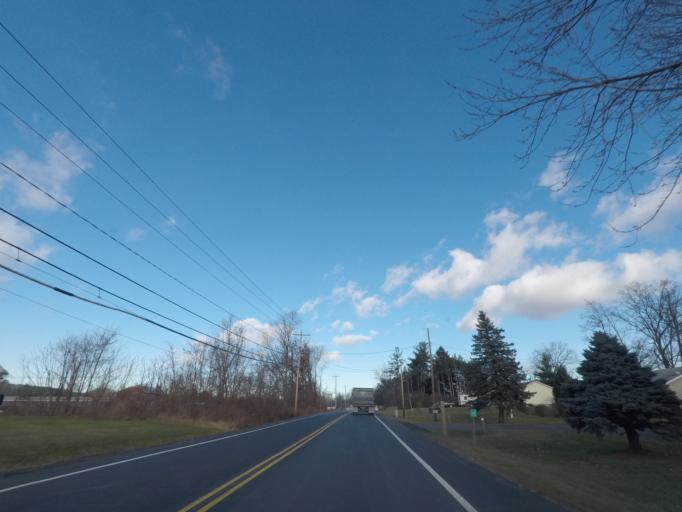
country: US
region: New York
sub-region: Saratoga County
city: Waterford
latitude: 42.8301
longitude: -73.6673
